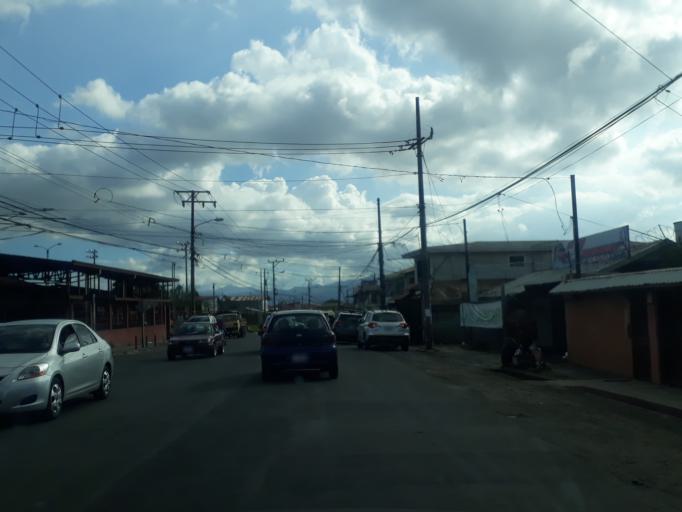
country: CR
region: San Jose
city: Ipis
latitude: 9.9856
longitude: -84.0270
